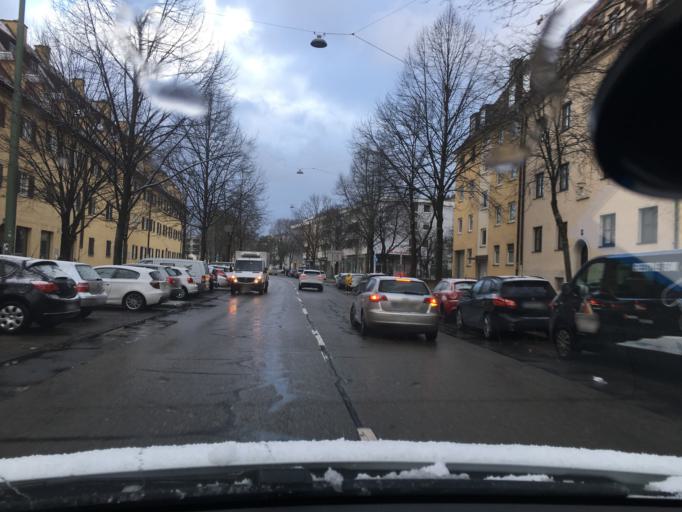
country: DE
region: Bavaria
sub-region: Upper Bavaria
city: Munich
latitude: 48.1031
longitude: 11.5460
